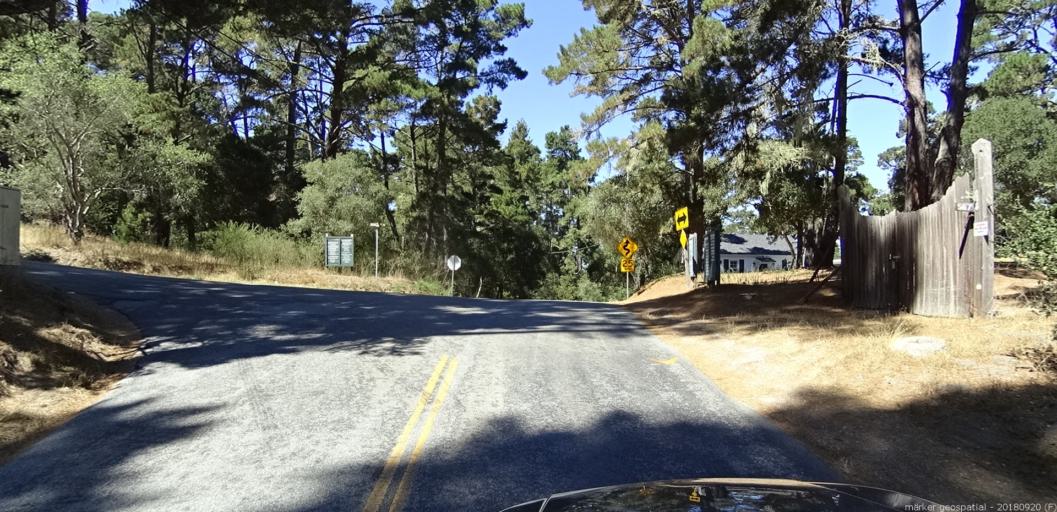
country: US
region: California
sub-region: Monterey County
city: Monterey
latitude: 36.5719
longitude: -121.8910
